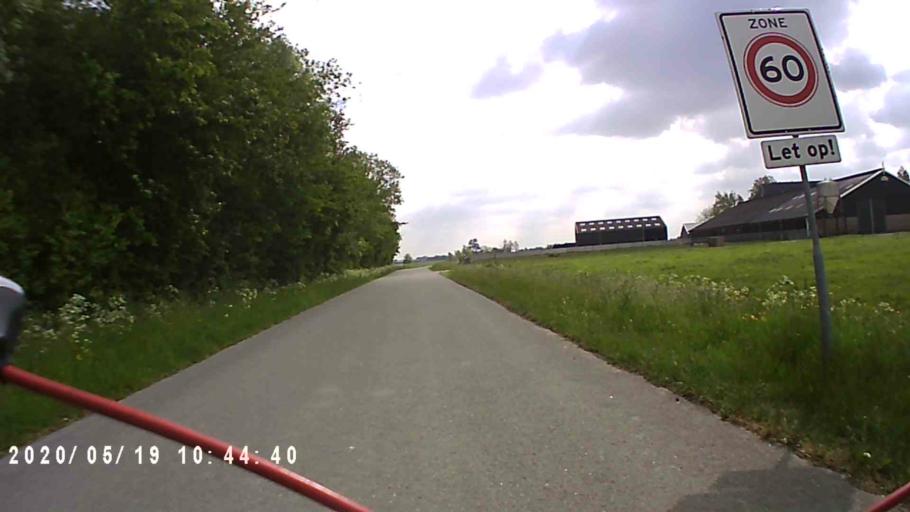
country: NL
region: Friesland
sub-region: Gemeente Kollumerland en Nieuwkruisland
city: Kollum
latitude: 53.2819
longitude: 6.2145
